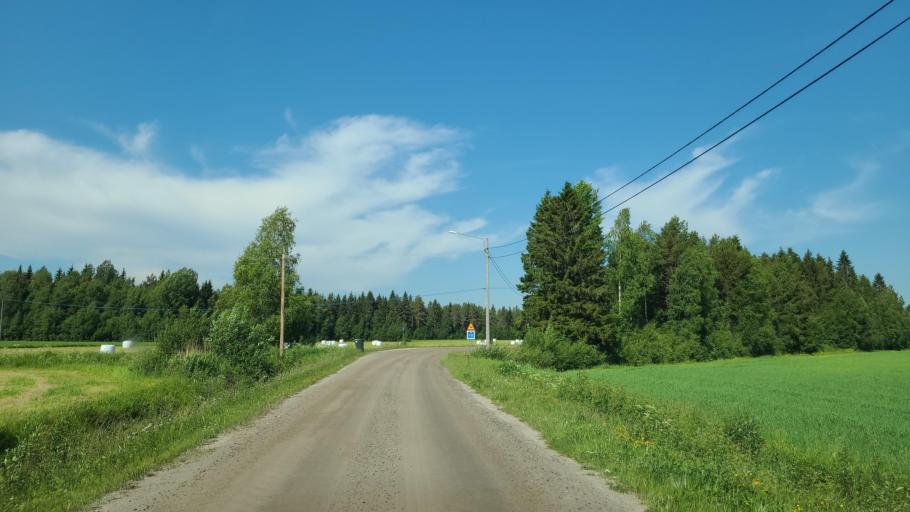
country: SE
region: Vaesterbotten
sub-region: Robertsfors Kommun
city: Robertsfors
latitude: 64.0820
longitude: 20.8483
